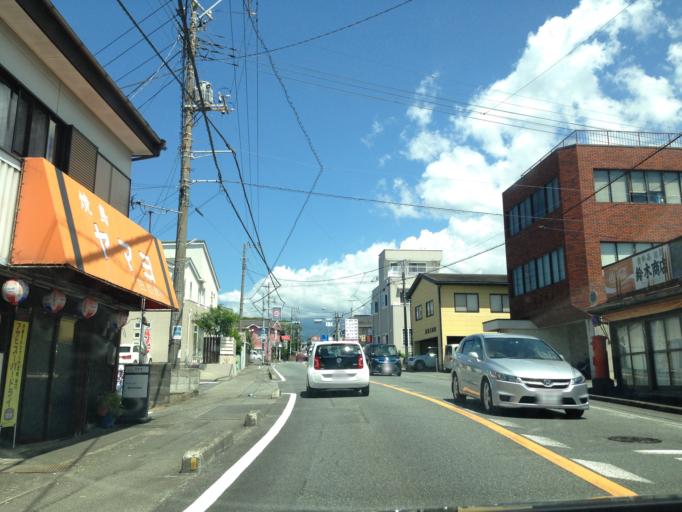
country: JP
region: Shizuoka
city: Fuji
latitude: 35.1667
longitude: 138.6890
